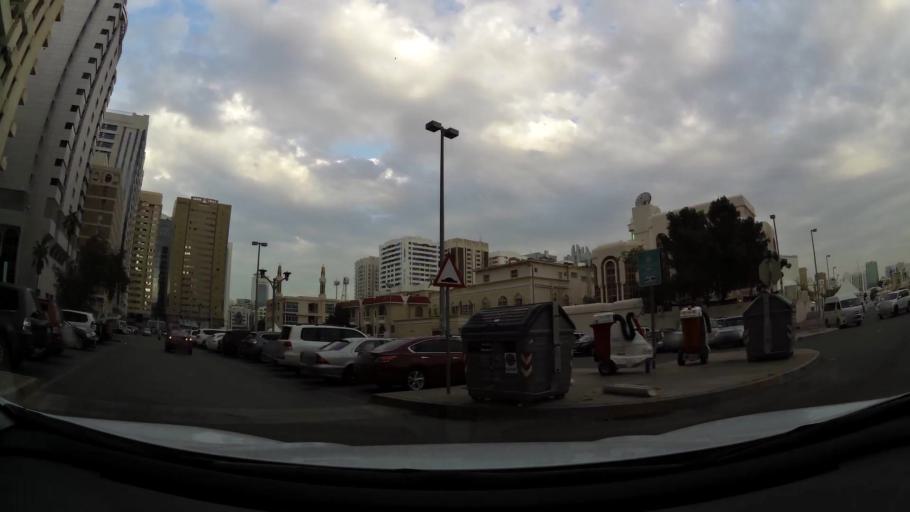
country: AE
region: Abu Dhabi
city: Abu Dhabi
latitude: 24.4885
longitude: 54.3677
